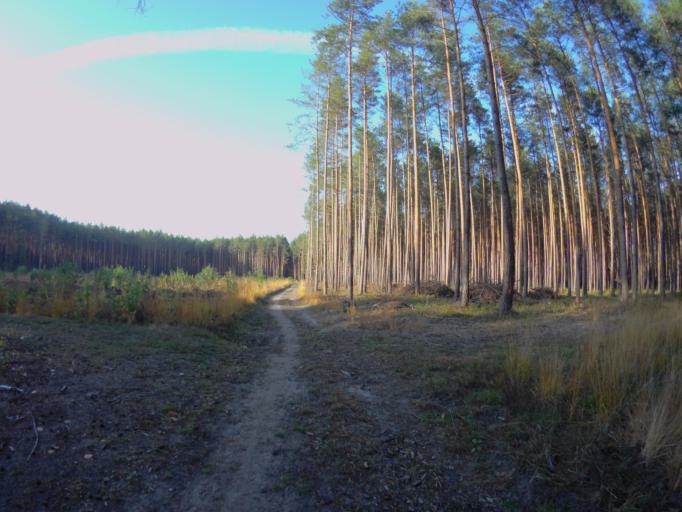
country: PL
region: Subcarpathian Voivodeship
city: Nowa Sarzyna
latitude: 50.3098
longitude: 22.3569
